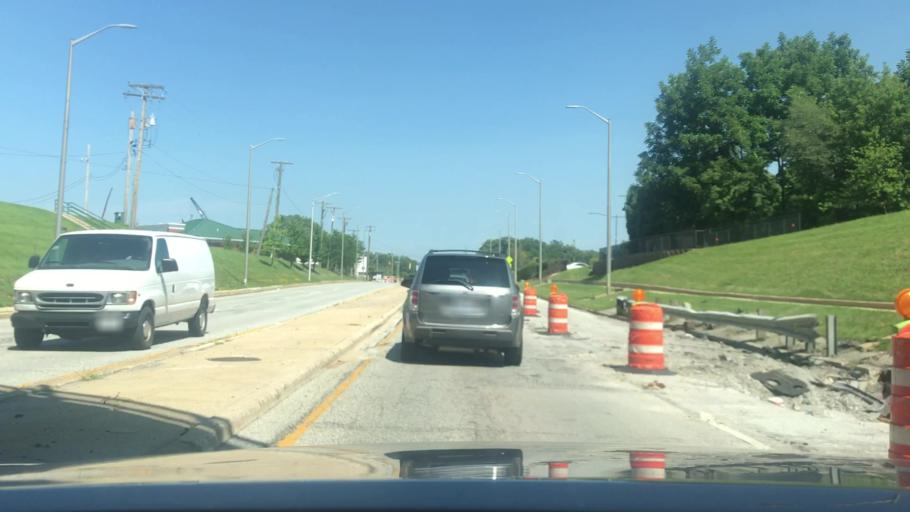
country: US
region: Illinois
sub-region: Cook County
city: Oak Forest
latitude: 41.6031
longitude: -87.7402
